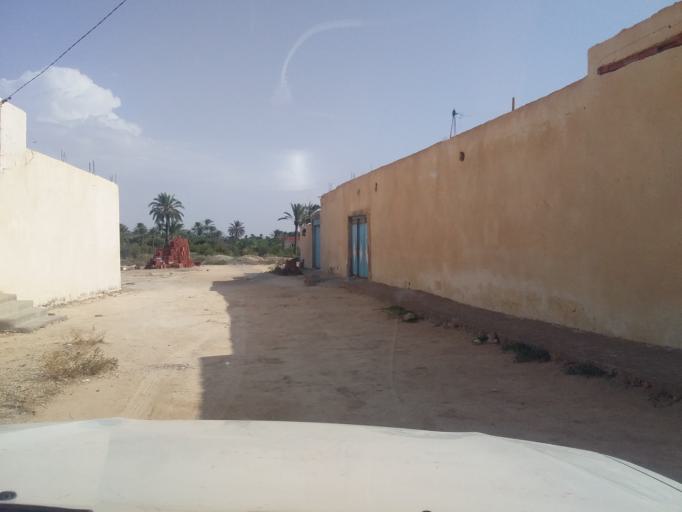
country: TN
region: Qabis
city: Gabes
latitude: 33.6421
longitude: 10.2978
